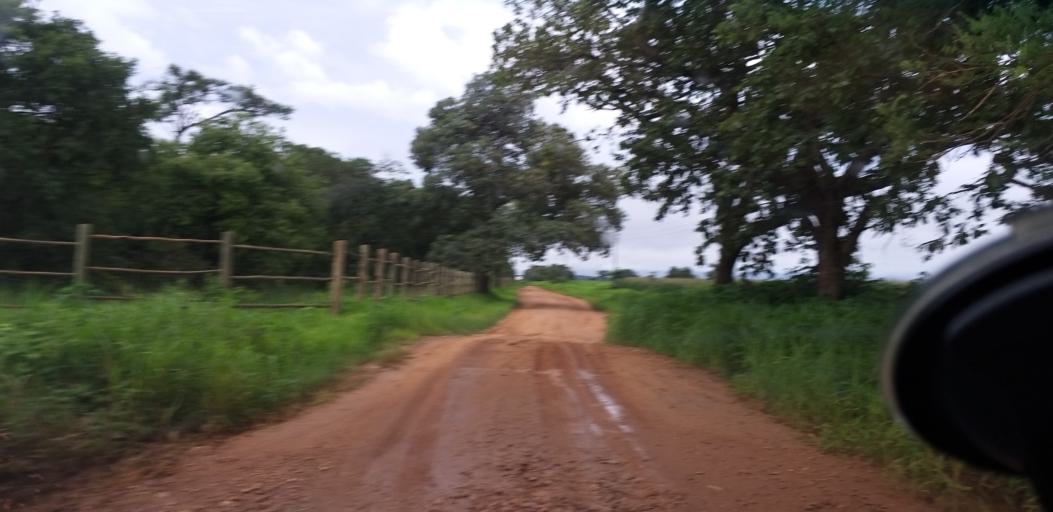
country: ZM
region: Lusaka
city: Lusaka
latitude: -15.5280
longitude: 28.3101
